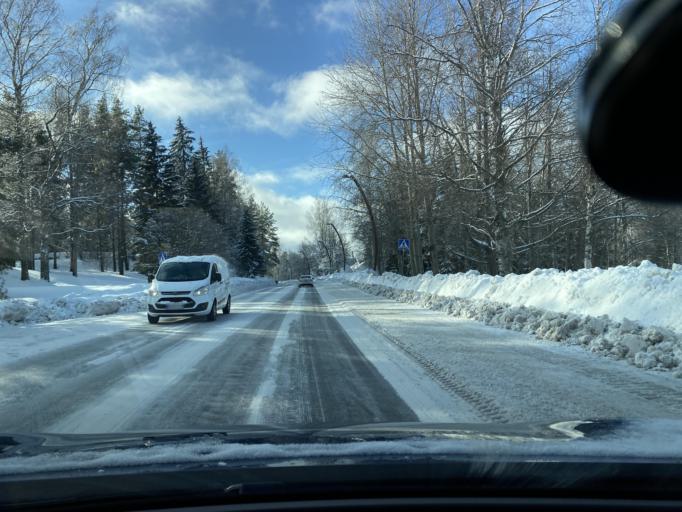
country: FI
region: Southern Savonia
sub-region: Mikkeli
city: Kangasniemi
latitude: 61.9938
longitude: 26.6468
